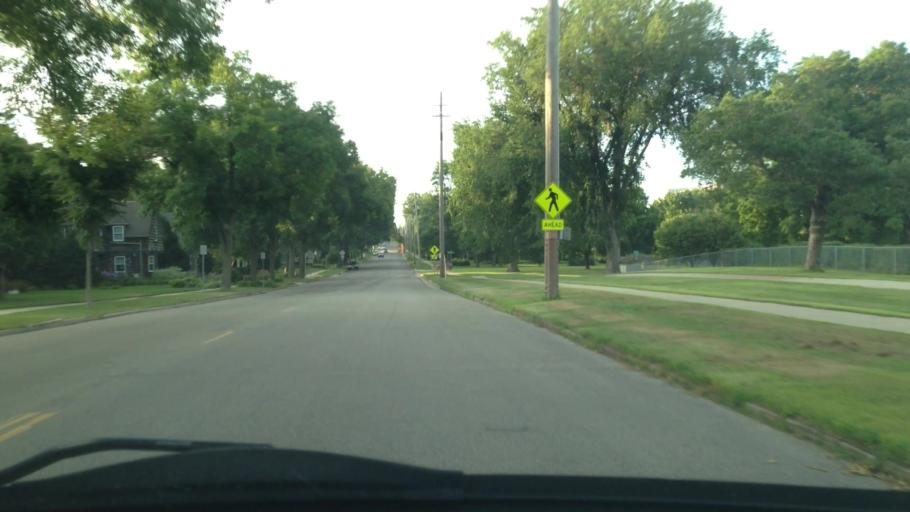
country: US
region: Minnesota
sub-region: Olmsted County
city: Rochester
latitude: 44.0118
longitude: -92.4713
